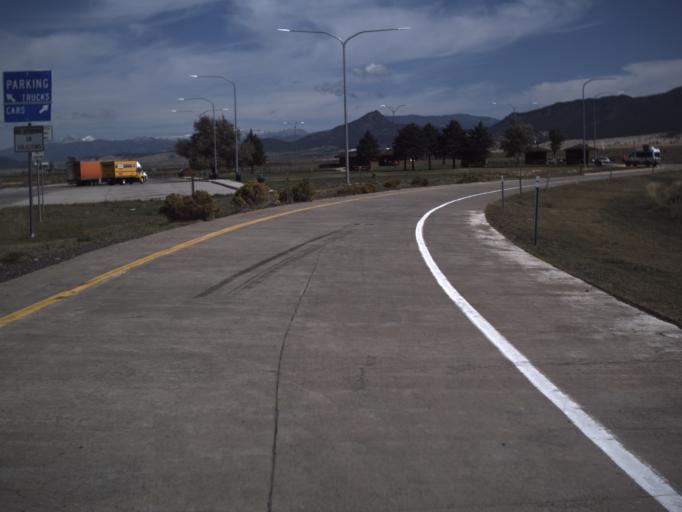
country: US
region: Utah
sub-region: Iron County
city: Parowan
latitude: 37.9794
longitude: -112.7377
